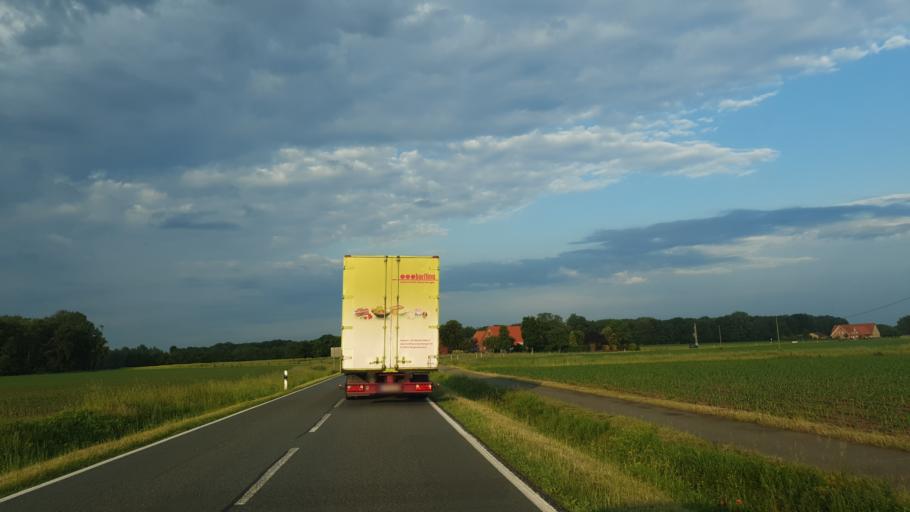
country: DE
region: North Rhine-Westphalia
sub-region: Regierungsbezirk Munster
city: Telgte
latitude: 52.0446
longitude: 7.7118
